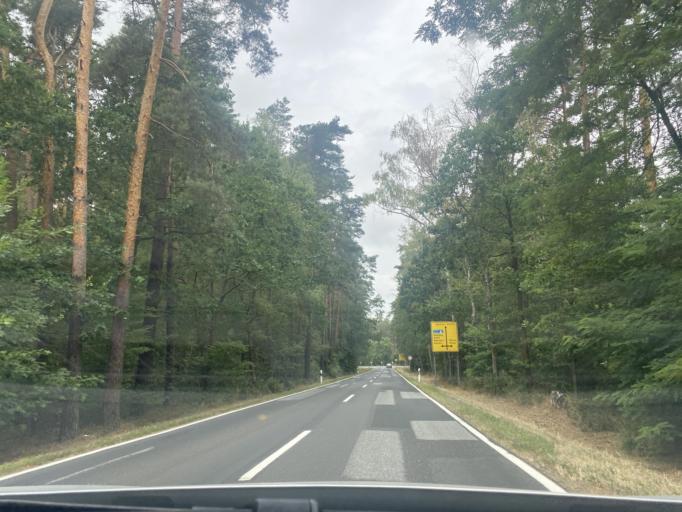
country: DE
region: Saxony
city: Mucka
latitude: 51.2831
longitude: 14.6595
